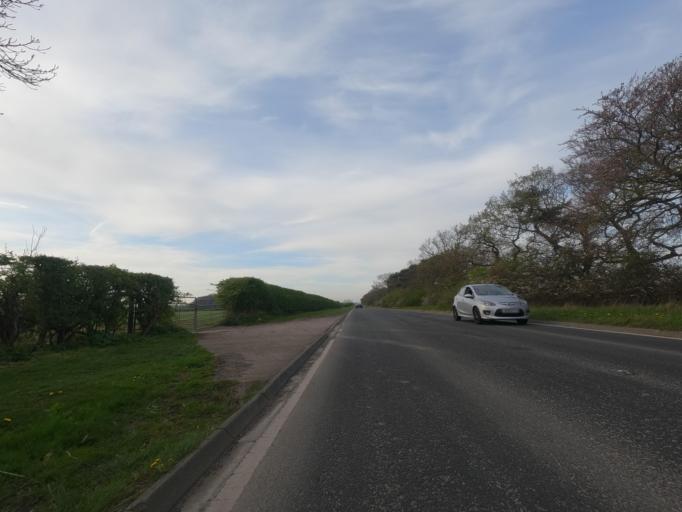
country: GB
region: England
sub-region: Newcastle upon Tyne
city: Dinnington
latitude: 55.0362
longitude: -1.6654
